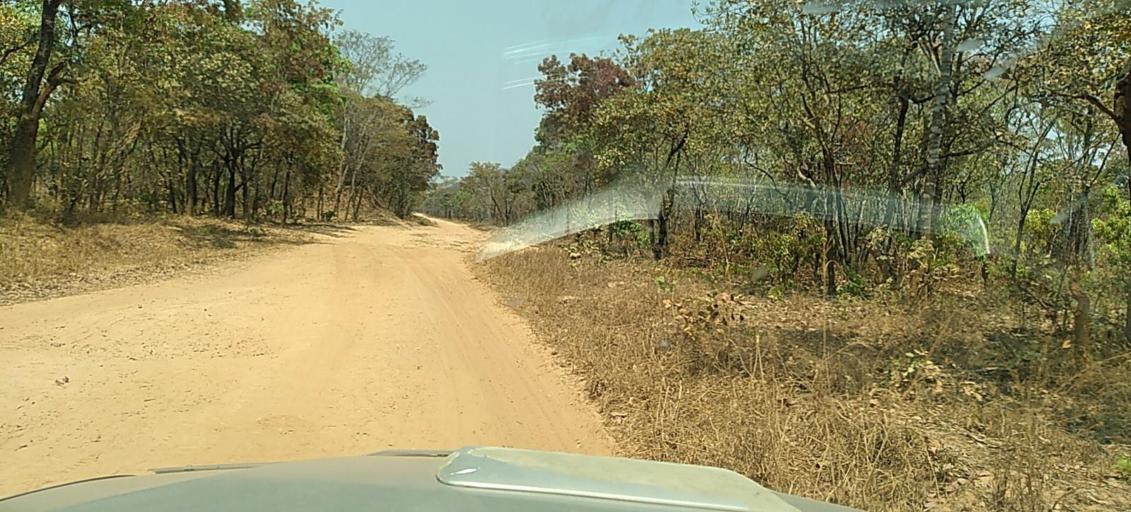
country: ZM
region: North-Western
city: Kasempa
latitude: -13.6559
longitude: 26.2602
